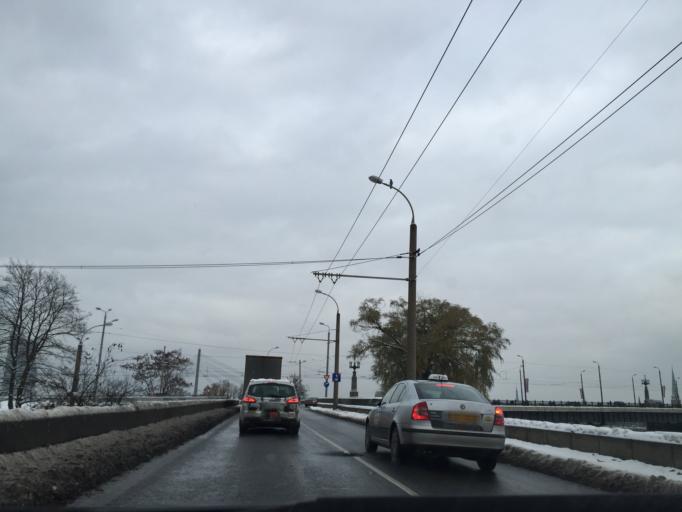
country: LV
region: Riga
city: Riga
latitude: 56.9421
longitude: 24.0982
